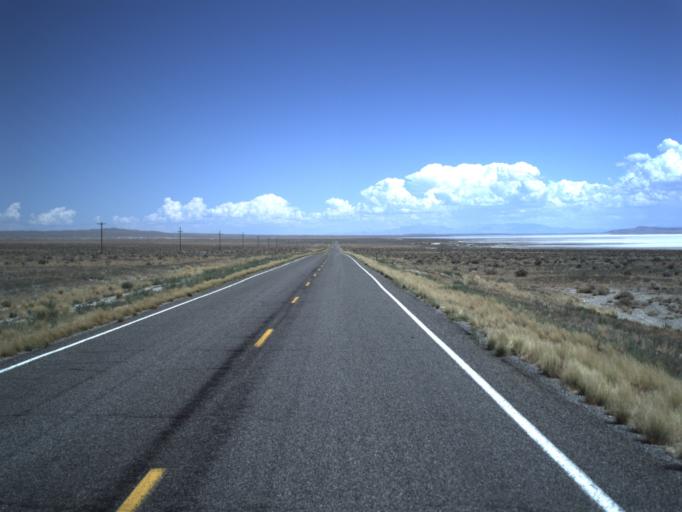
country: US
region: Utah
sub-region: Millard County
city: Delta
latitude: 39.0728
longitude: -113.2160
